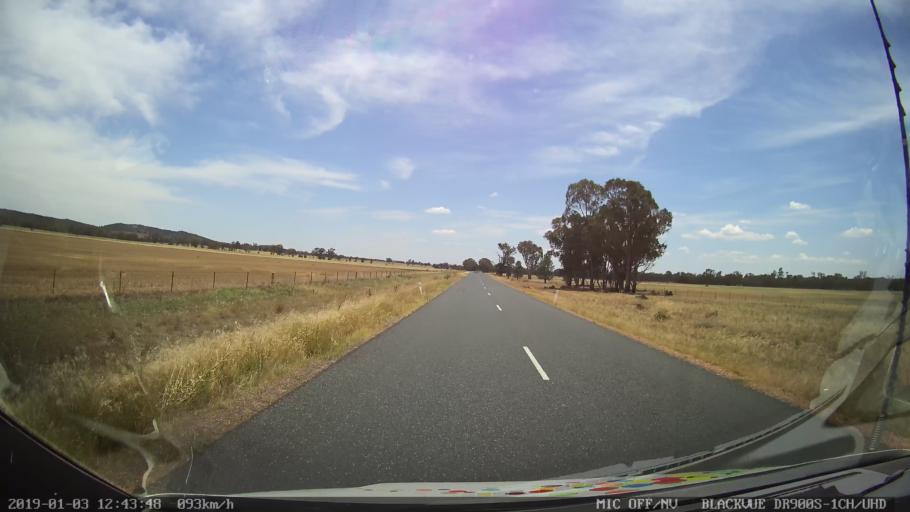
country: AU
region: New South Wales
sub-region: Weddin
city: Grenfell
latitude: -33.7702
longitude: 148.2145
